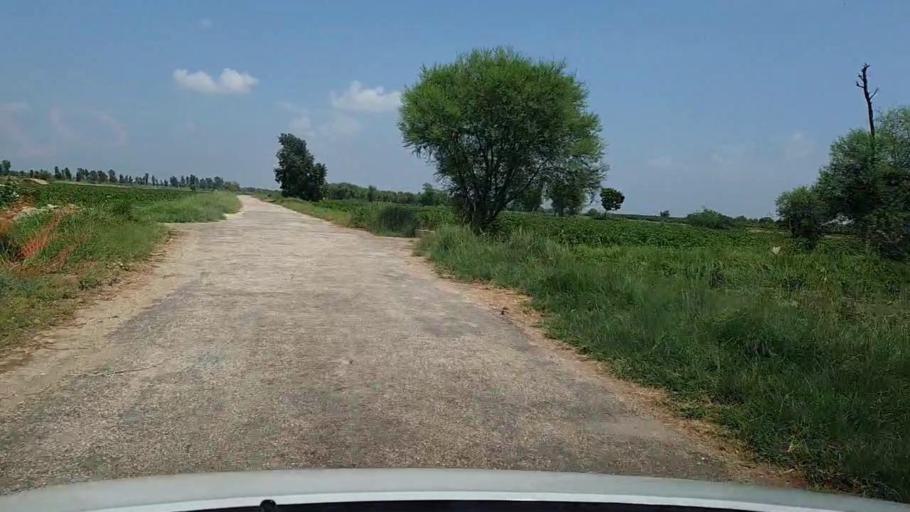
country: PK
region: Sindh
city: Bhiria
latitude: 26.9750
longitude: 68.2112
